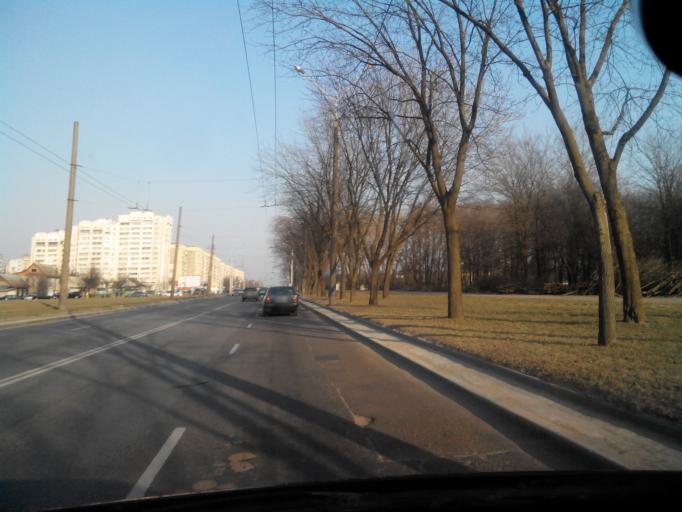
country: BY
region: Minsk
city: Novoye Medvezhino
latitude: 53.8938
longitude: 27.4765
